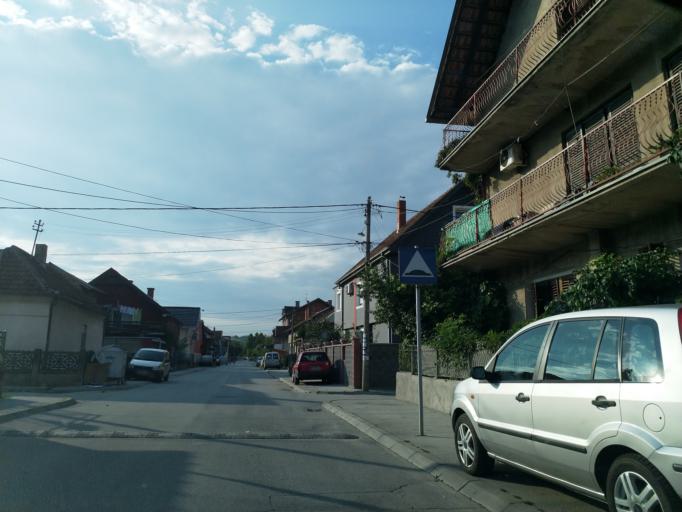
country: RS
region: Central Serbia
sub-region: Pomoravski Okrug
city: Jagodina
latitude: 43.9808
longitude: 21.2454
